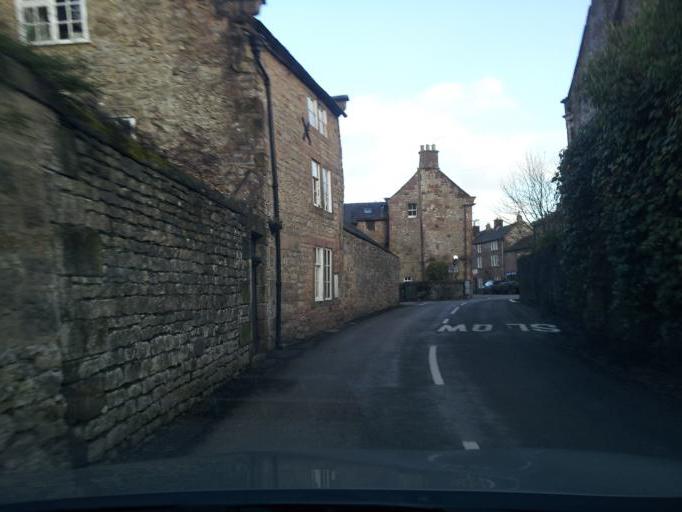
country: GB
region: England
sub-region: Derbyshire
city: Bakewell
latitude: 53.1419
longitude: -1.6432
